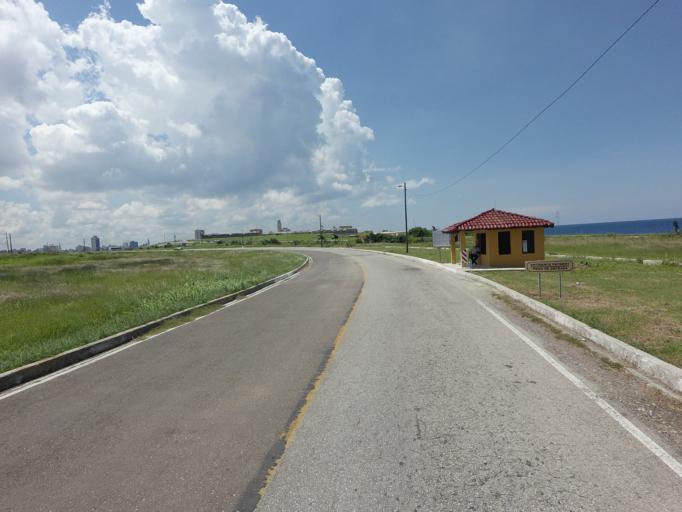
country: CU
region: La Habana
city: Centro Habana
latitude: 23.1522
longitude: -82.3527
